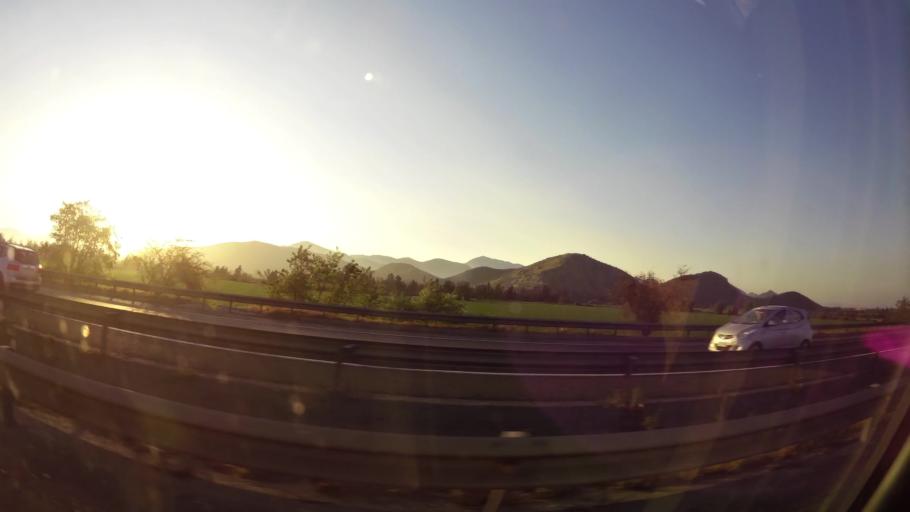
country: CL
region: Santiago Metropolitan
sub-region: Provincia de Talagante
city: Penaflor
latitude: -33.5504
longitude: -70.8098
